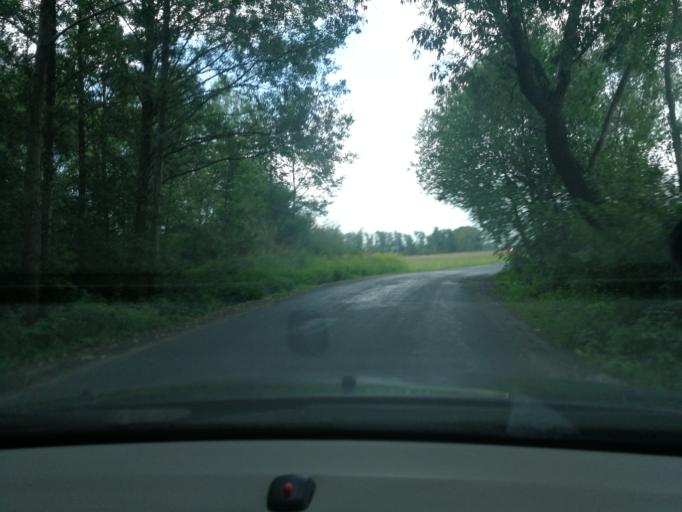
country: PL
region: Masovian Voivodeship
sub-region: Powiat warszawski zachodni
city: Bieniewice
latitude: 52.1147
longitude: 20.5557
